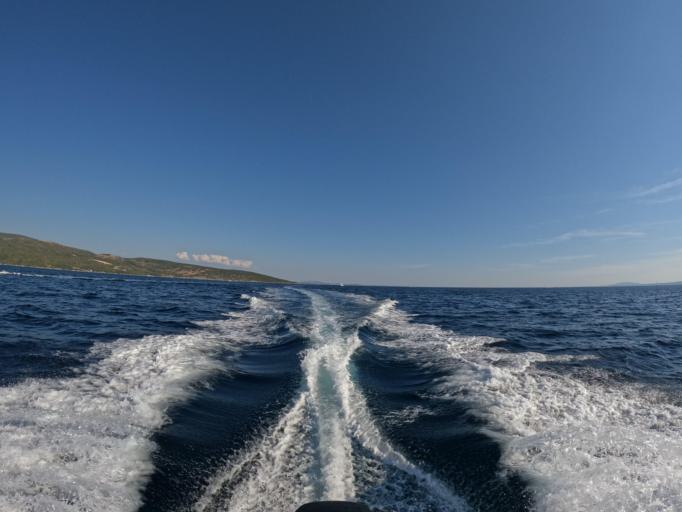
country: HR
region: Primorsko-Goranska
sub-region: Grad Krk
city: Krk
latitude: 45.0018
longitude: 14.5968
